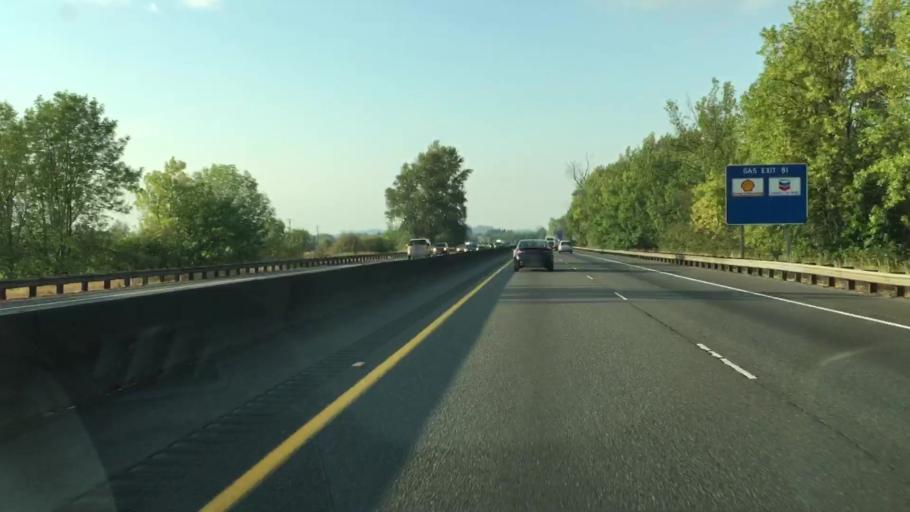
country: US
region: Washington
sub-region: Lewis County
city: Chehalis
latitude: 46.6884
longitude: -122.9703
